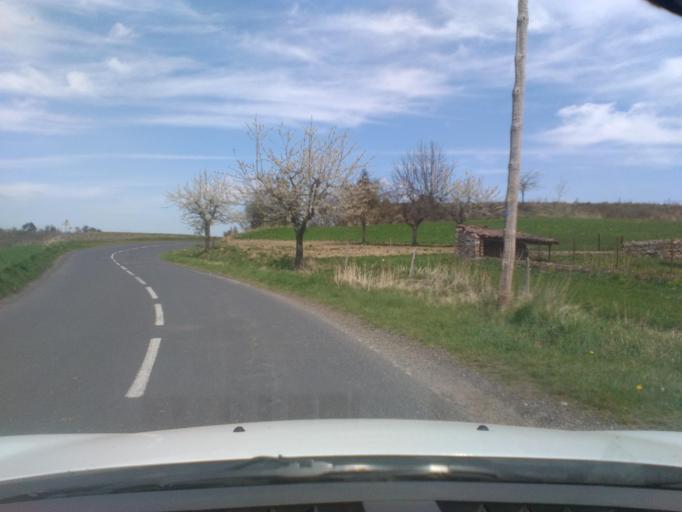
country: FR
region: Auvergne
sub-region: Departement de la Haute-Loire
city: La Seauve-sur-Semene
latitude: 45.3107
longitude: 4.2312
